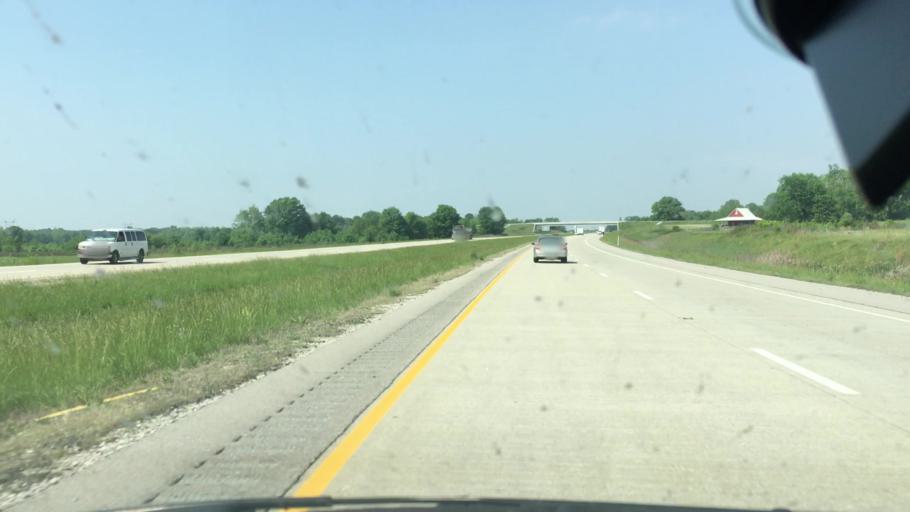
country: US
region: Indiana
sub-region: Daviess County
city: Washington
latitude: 38.6299
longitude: -87.1364
